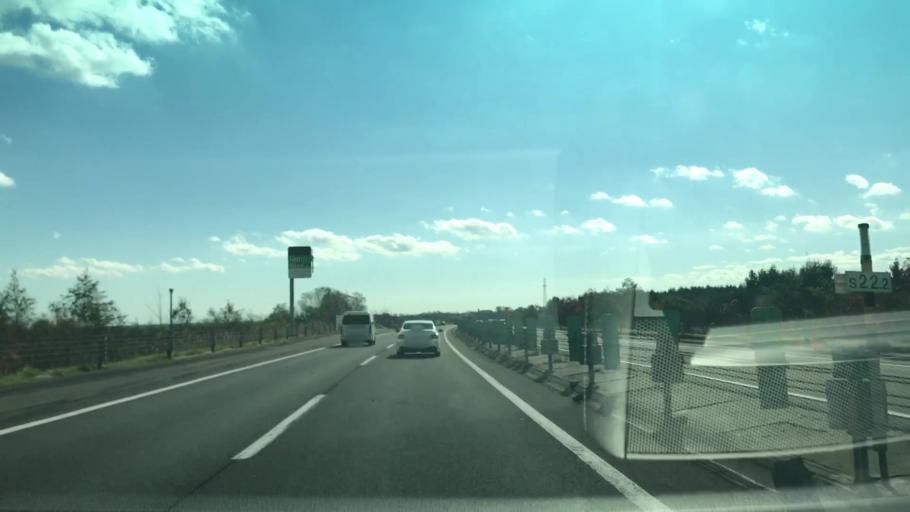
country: JP
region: Hokkaido
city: Kitahiroshima
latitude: 42.9075
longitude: 141.5506
